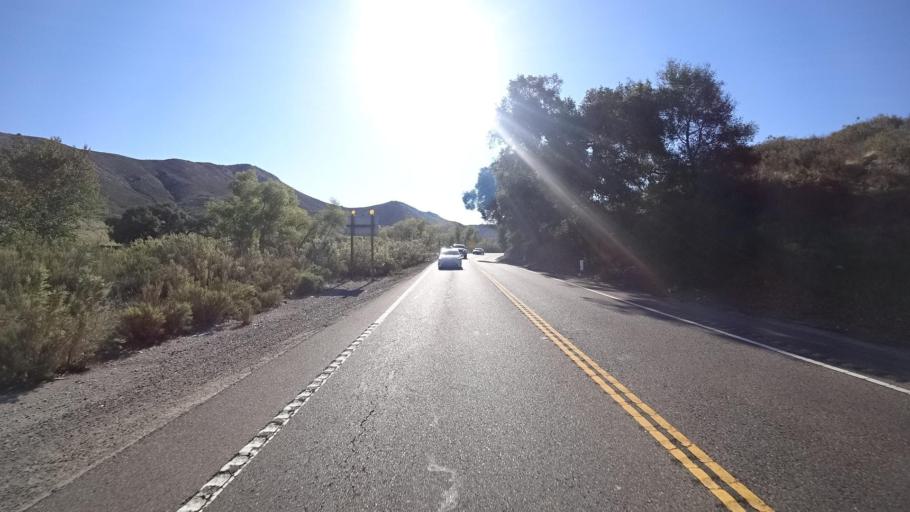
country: US
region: California
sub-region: San Diego County
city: Jamul
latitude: 32.6631
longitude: -116.8133
